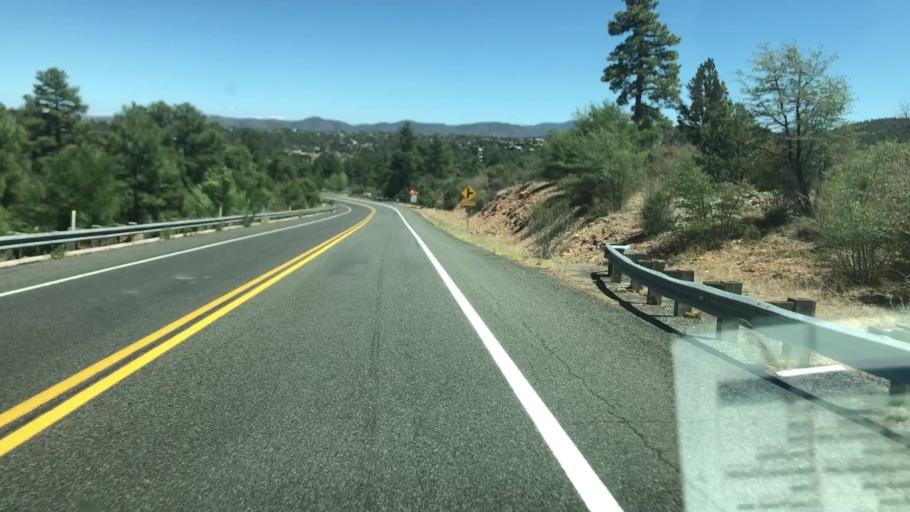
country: US
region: Arizona
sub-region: Yavapai County
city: Prescott
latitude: 34.5793
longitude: -112.5302
